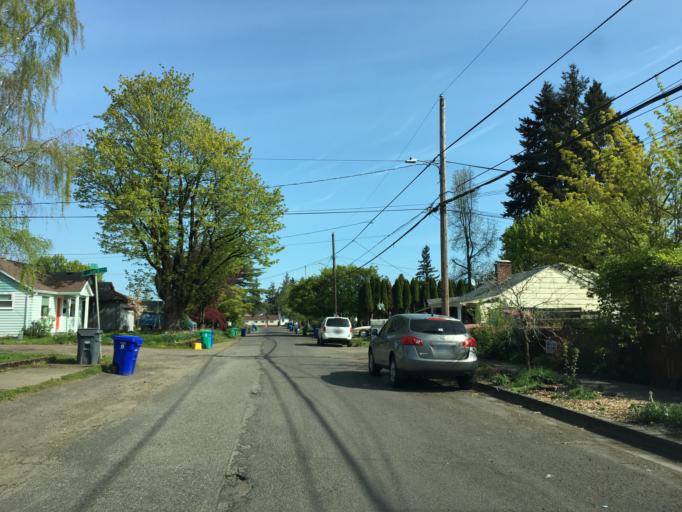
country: US
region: Oregon
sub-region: Multnomah County
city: Lents
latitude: 45.5246
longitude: -122.5684
